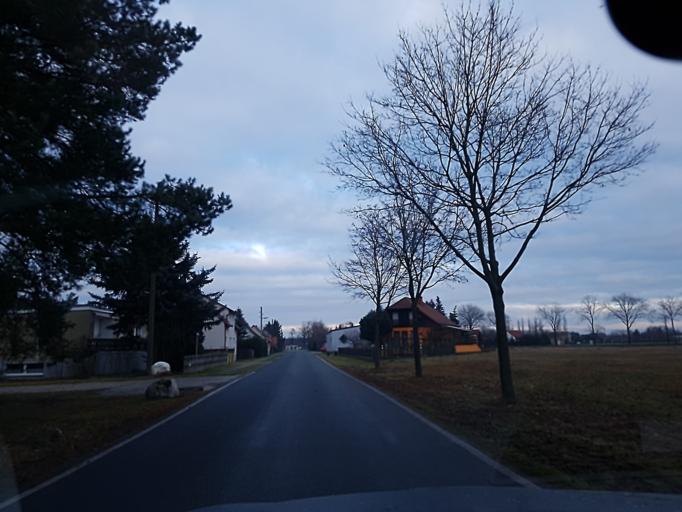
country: DE
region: Brandenburg
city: Schilda
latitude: 51.5748
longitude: 13.3562
